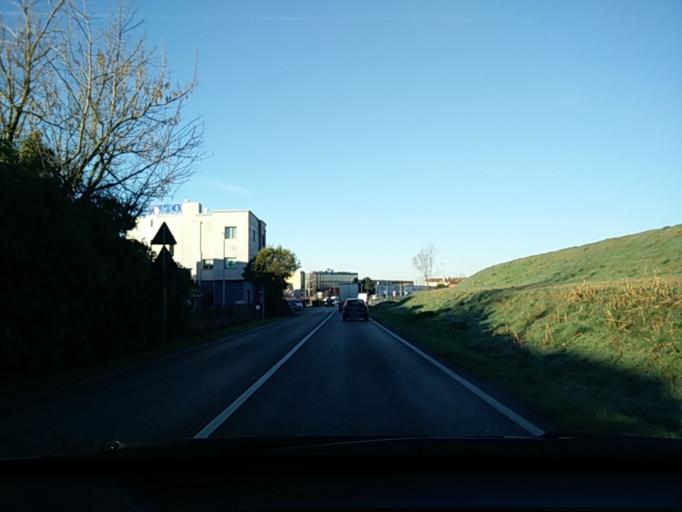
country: IT
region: Veneto
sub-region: Provincia di Venezia
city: San Dona di Piave
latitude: 45.6228
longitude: 12.5593
